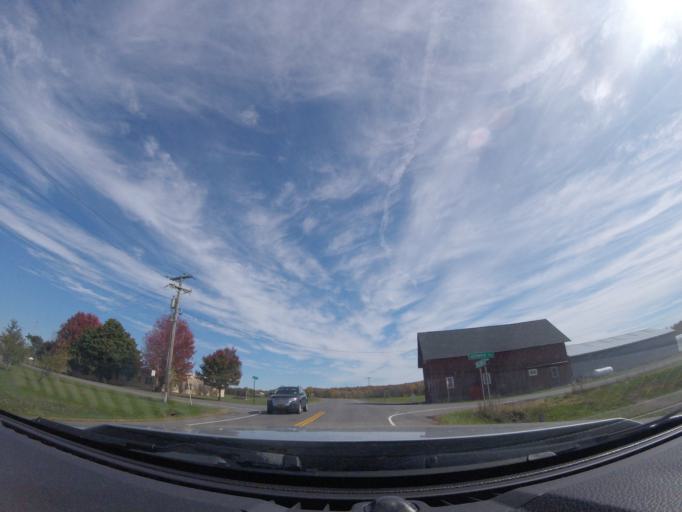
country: US
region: New York
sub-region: Tompkins County
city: Dryden
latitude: 42.5178
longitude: -76.3361
